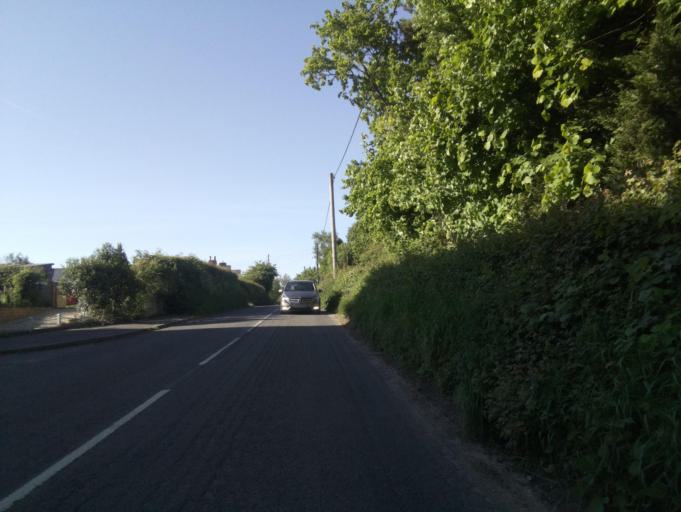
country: GB
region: England
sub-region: Somerset
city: Crewkerne
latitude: 50.8581
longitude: -2.8309
